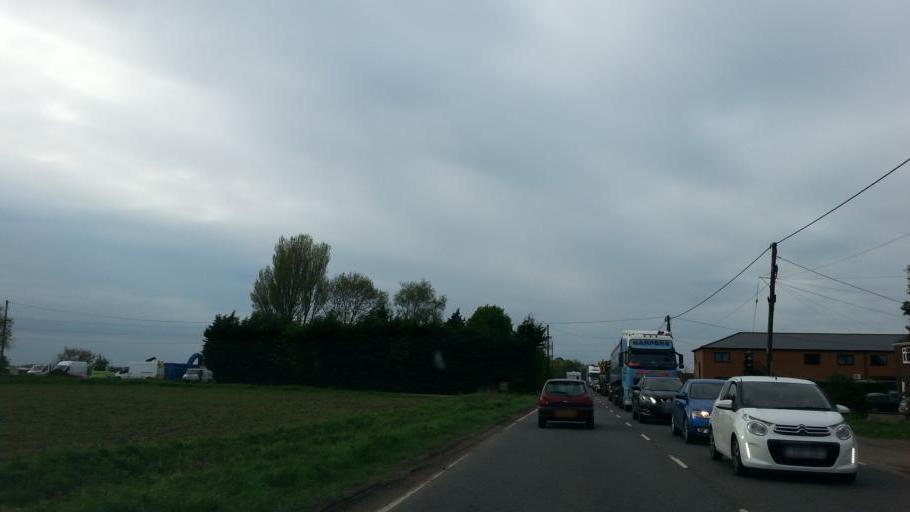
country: GB
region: England
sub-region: Cambridgeshire
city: March
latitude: 52.5704
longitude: 0.0593
